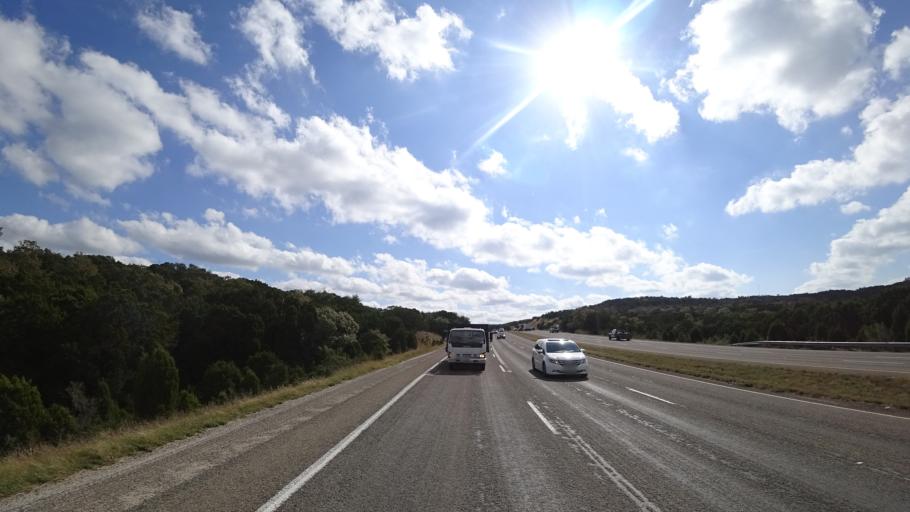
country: US
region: Texas
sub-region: Travis County
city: Barton Creek
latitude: 30.2676
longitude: -97.8938
